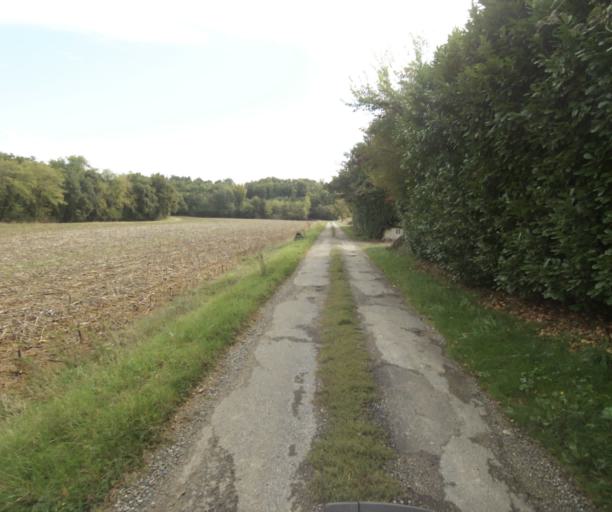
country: FR
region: Midi-Pyrenees
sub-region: Departement du Tarn-et-Garonne
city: Verdun-sur-Garonne
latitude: 43.8674
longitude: 1.1878
